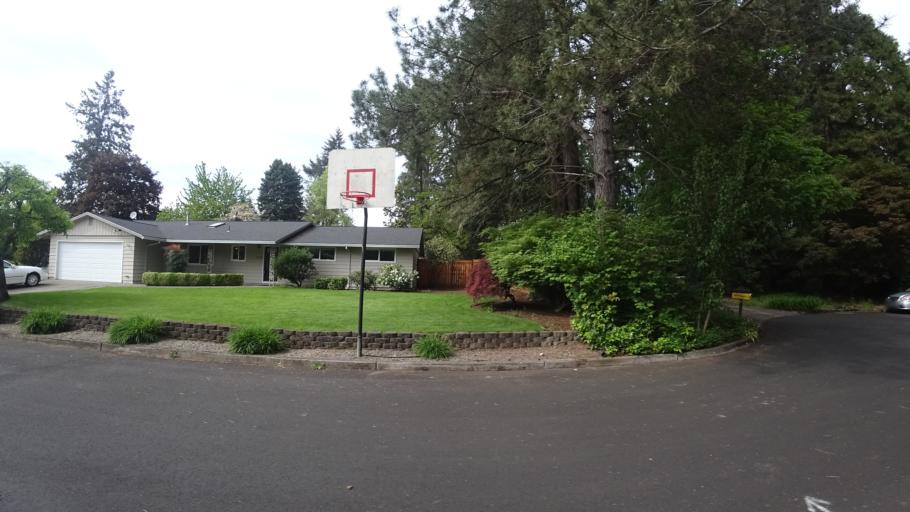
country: US
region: Oregon
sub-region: Washington County
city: Hillsboro
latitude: 45.5115
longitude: -122.9439
